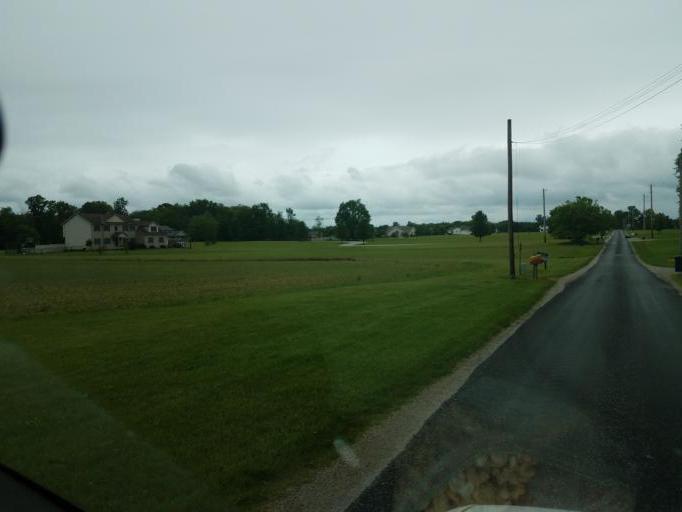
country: US
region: Ohio
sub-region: Marion County
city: Marion
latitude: 40.5360
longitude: -83.0145
